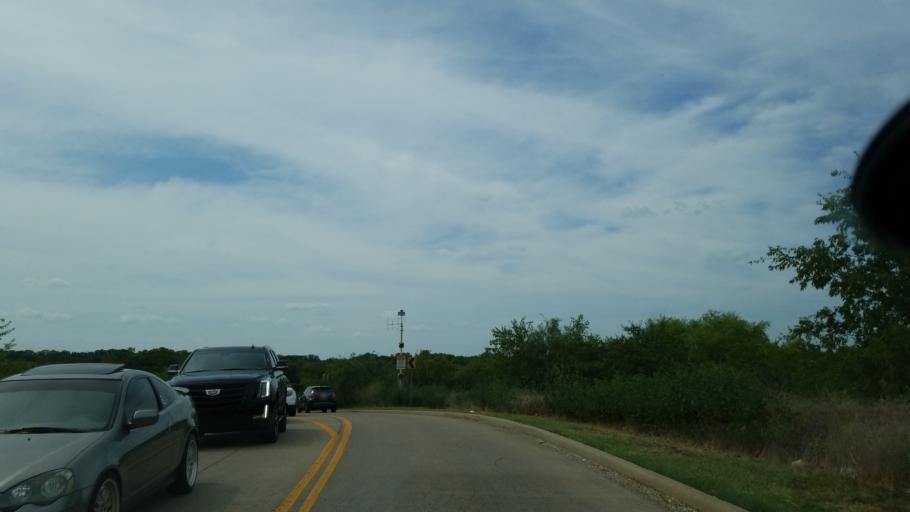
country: US
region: Texas
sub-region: Tarrant County
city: Arlington
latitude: 32.7789
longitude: -97.1354
